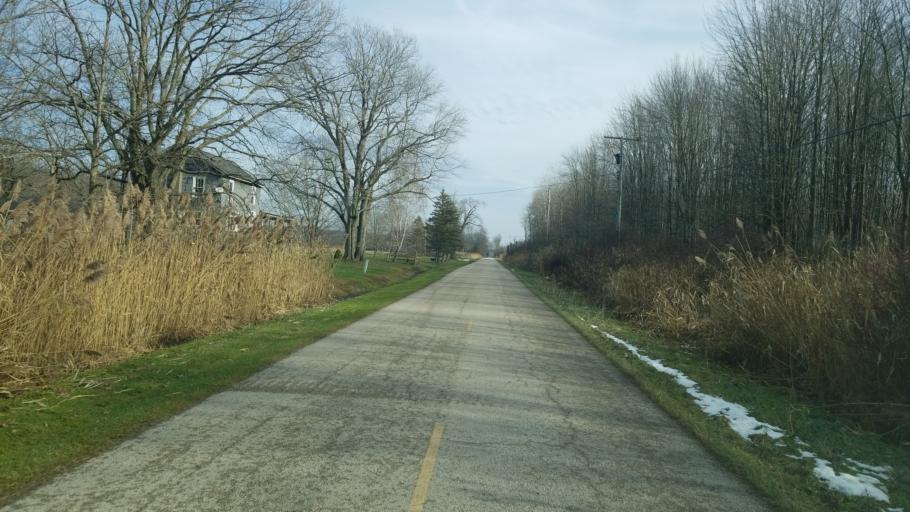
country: US
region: Ohio
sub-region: Ashtabula County
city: Roaming Shores
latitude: 41.6434
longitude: -80.7447
